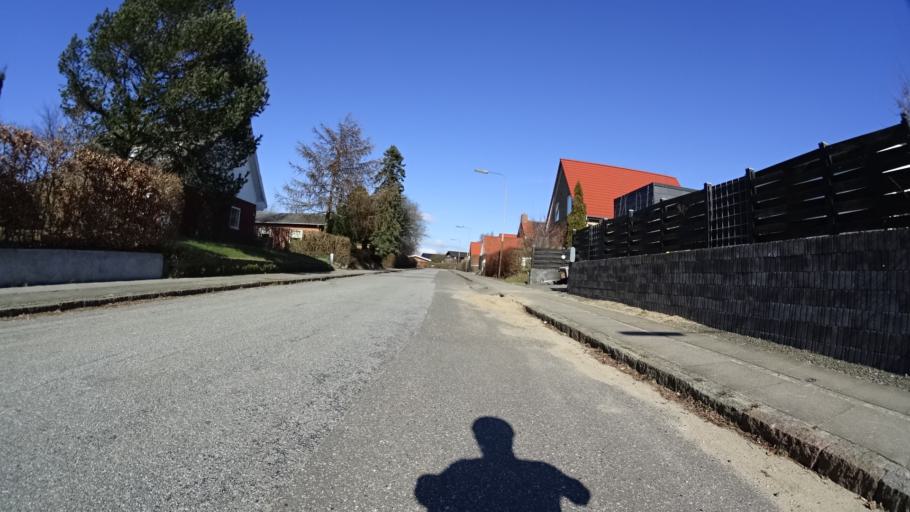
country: DK
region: Central Jutland
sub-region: Arhus Kommune
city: Arhus
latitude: 56.1712
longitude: 10.1676
